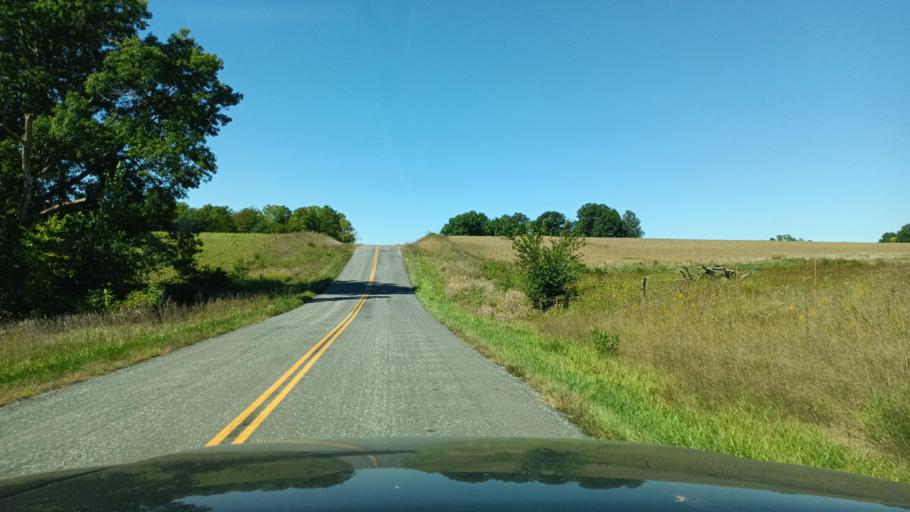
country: US
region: Missouri
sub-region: Adair County
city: Kirksville
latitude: 40.3301
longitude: -92.5387
